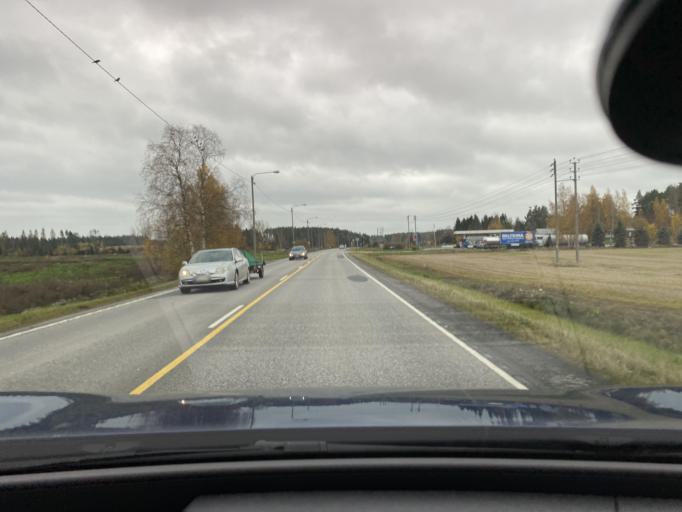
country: FI
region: Varsinais-Suomi
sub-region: Vakka-Suomi
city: Pyhaeranta
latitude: 60.9788
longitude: 21.5915
